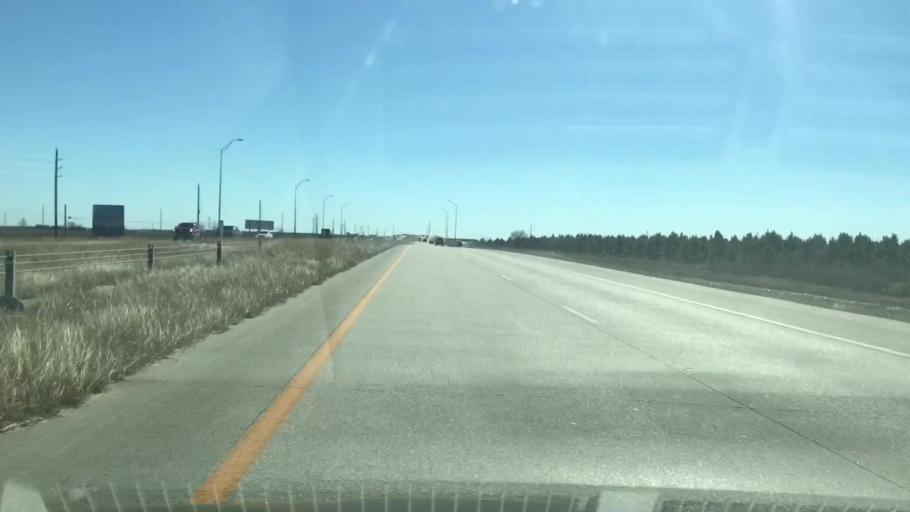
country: US
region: Texas
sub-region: Harris County
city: Cypress
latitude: 29.9307
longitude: -95.7632
